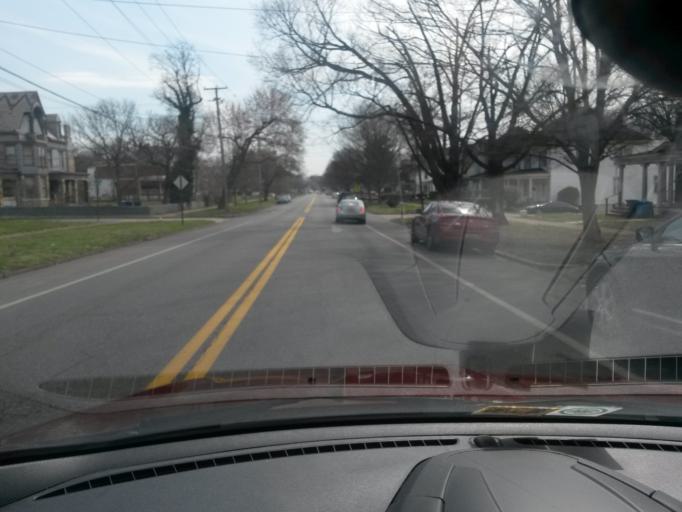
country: US
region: Virginia
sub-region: City of Roanoke
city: Roanoke
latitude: 37.2735
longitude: -79.9684
